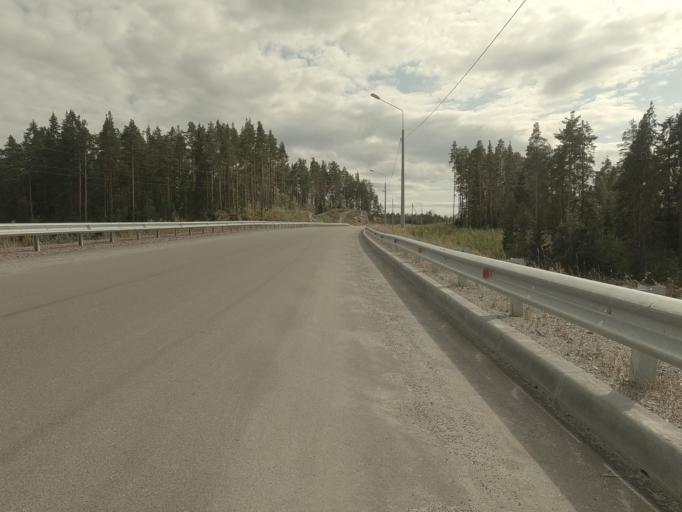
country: RU
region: Leningrad
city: Kamennogorsk
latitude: 60.9625
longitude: 29.1416
